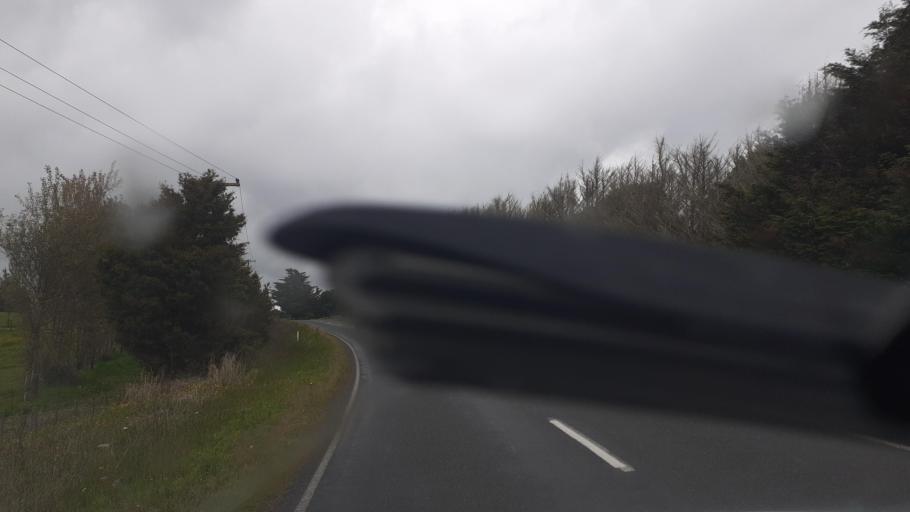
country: NZ
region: Northland
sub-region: Far North District
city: Waimate North
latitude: -35.2787
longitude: 173.8309
